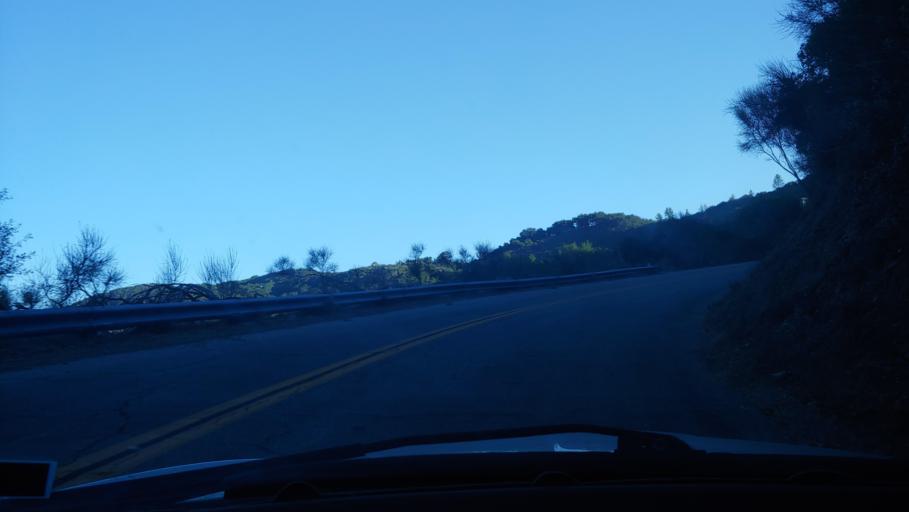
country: US
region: California
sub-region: Santa Barbara County
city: Goleta
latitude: 34.5195
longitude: -119.8296
